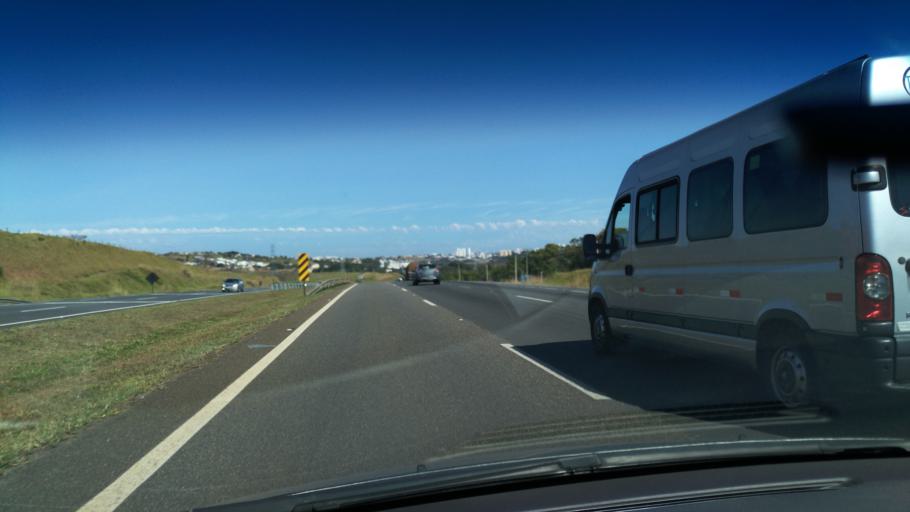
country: BR
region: Sao Paulo
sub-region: Jaguariuna
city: Jaguariuna
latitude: -22.7985
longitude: -47.0325
